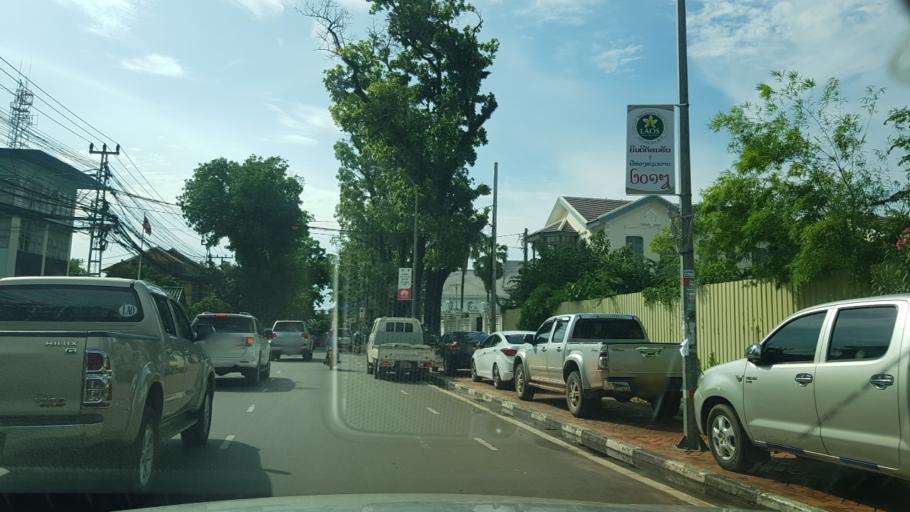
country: LA
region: Vientiane
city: Vientiane
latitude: 17.9641
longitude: 102.6082
